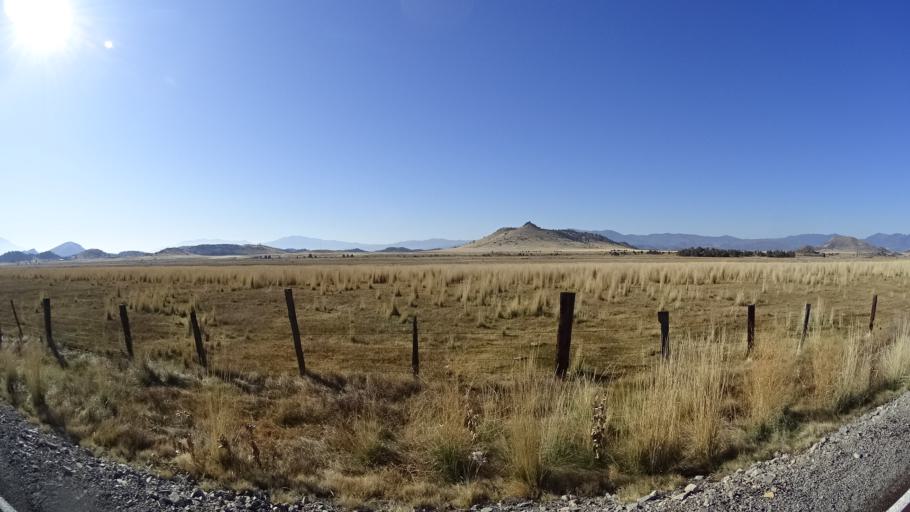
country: US
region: California
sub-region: Siskiyou County
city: Montague
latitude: 41.7161
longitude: -122.4443
